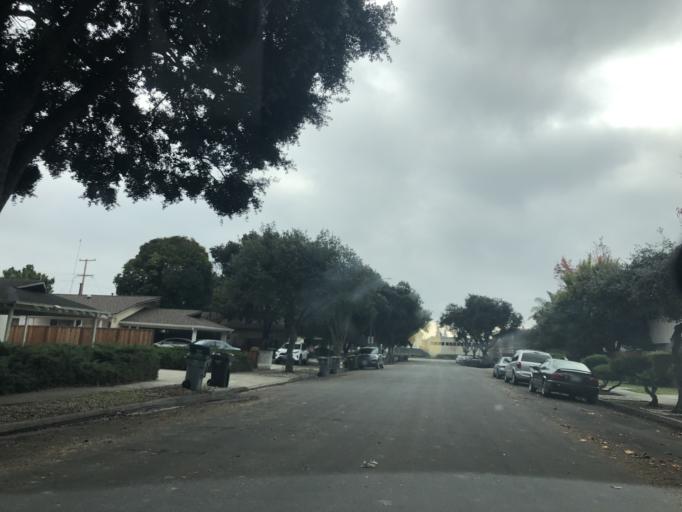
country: US
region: California
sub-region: Santa Clara County
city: Sunnyvale
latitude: 37.3897
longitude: -122.0090
